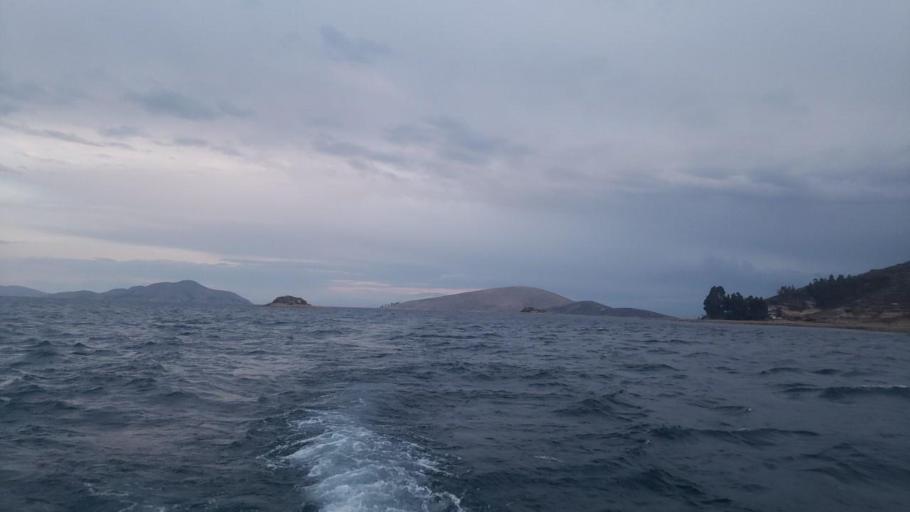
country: BO
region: La Paz
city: San Pablo
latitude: -16.2354
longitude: -68.8303
